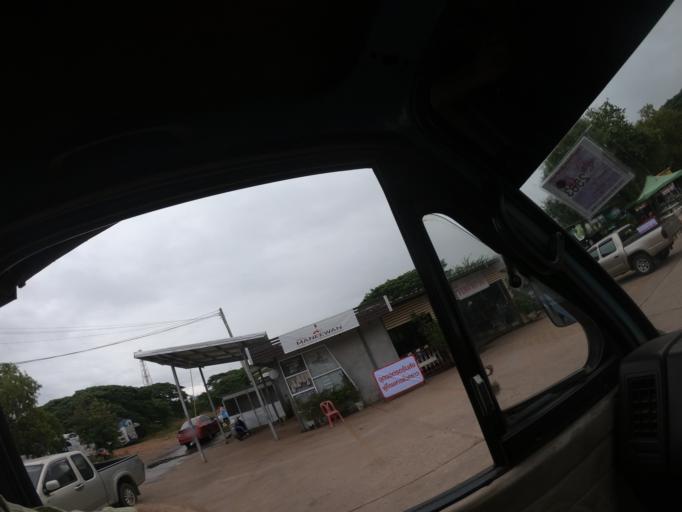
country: TH
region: Roi Et
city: Roi Et
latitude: 16.0533
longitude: 103.6401
